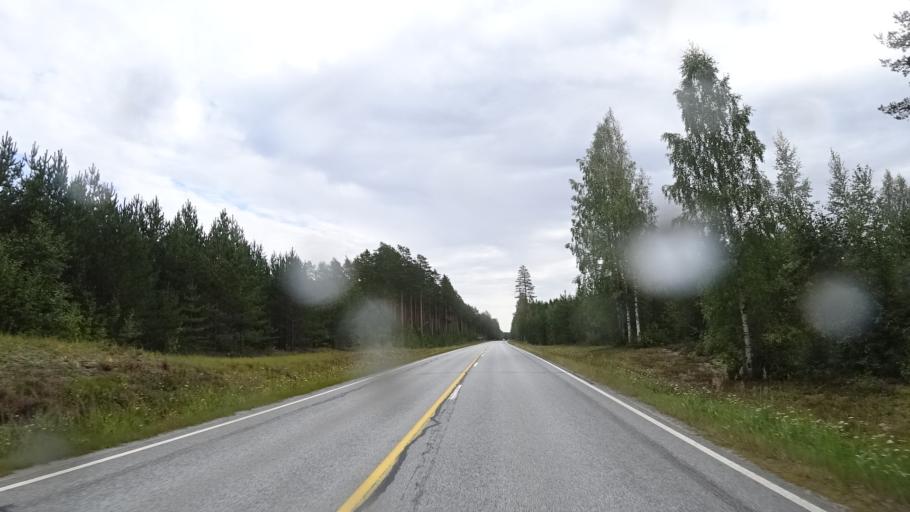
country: FI
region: North Karelia
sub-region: Keski-Karjala
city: Raeaekkylae
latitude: 62.1106
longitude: 29.7248
